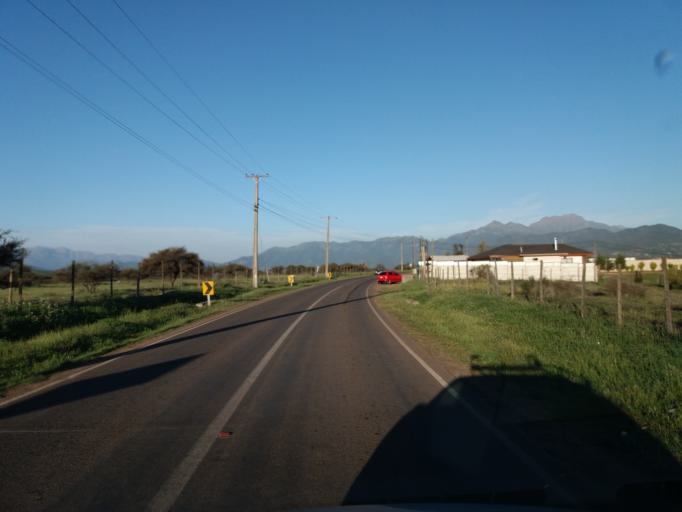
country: CL
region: Valparaiso
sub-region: Provincia de Quillota
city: Quillota
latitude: -32.9168
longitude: -71.3314
